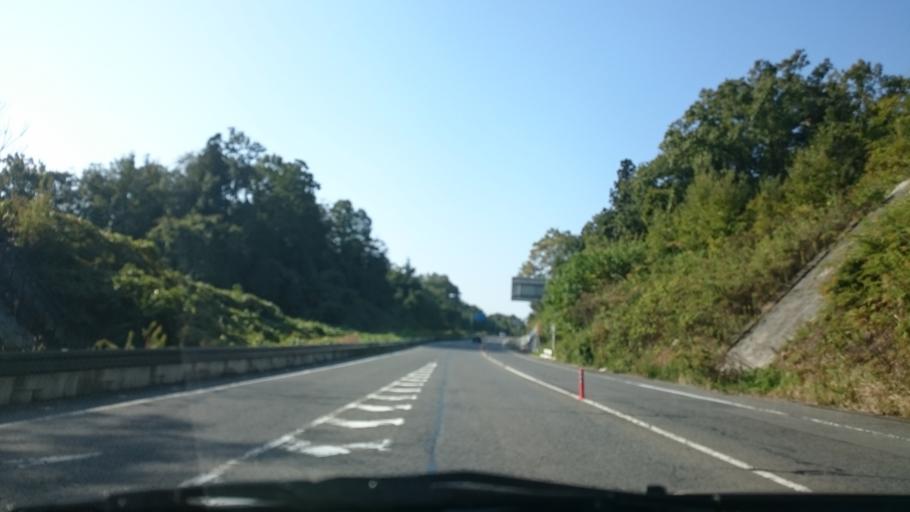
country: JP
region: Gifu
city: Minokamo
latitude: 35.4754
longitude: 137.0399
